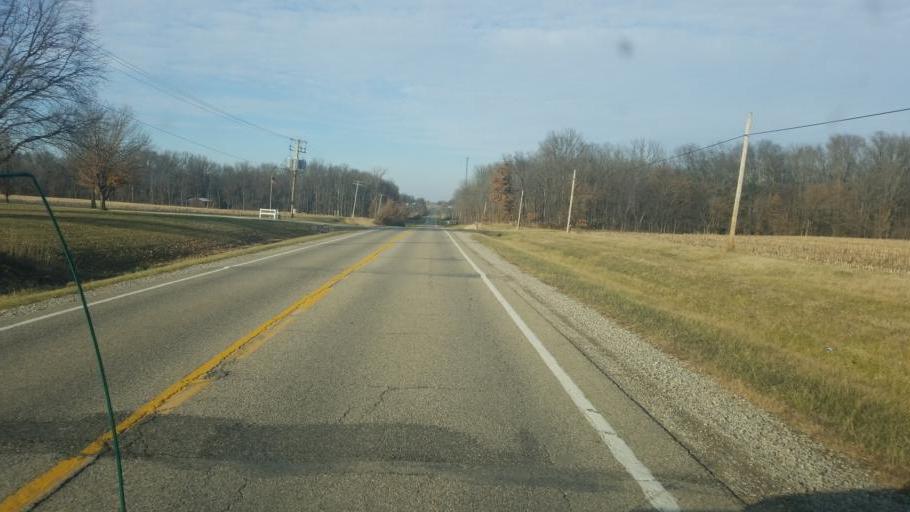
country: US
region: Illinois
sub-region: Lawrence County
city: Lawrenceville
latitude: 38.6605
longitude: -87.6943
